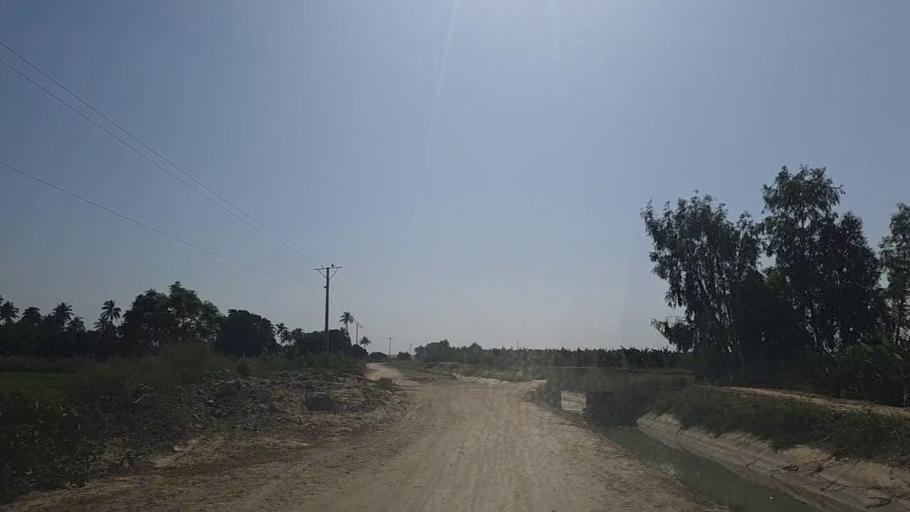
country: PK
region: Sindh
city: Thatta
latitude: 24.6396
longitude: 67.8907
